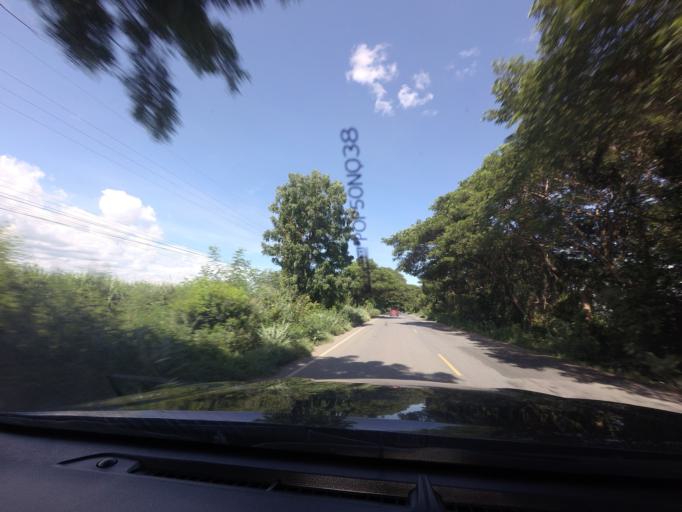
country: TH
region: Kanchanaburi
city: Phanom Thuan
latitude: 14.1690
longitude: 99.8369
